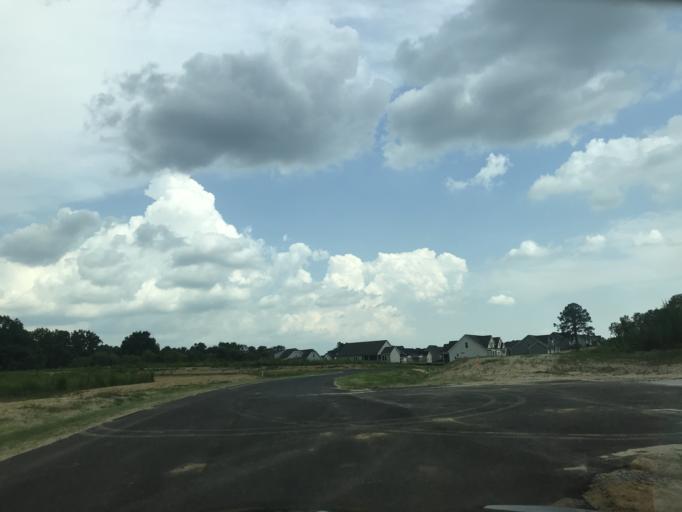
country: US
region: North Carolina
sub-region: Johnston County
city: Four Oaks
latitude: 35.5203
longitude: -78.5317
